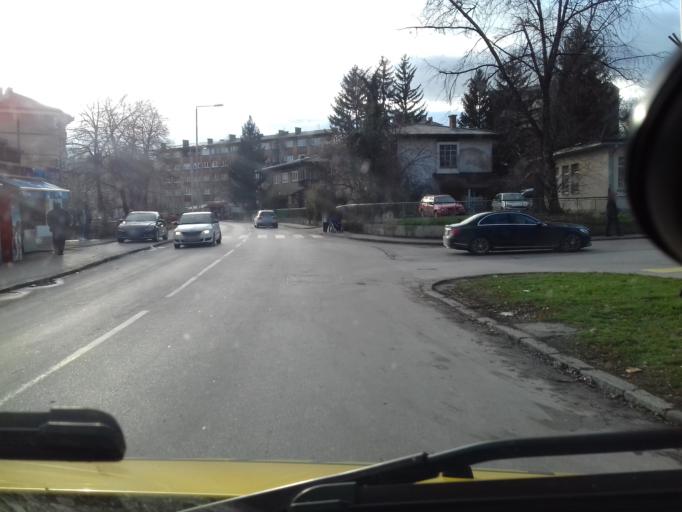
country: BA
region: Federation of Bosnia and Herzegovina
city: Zenica
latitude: 44.2071
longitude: 17.9242
